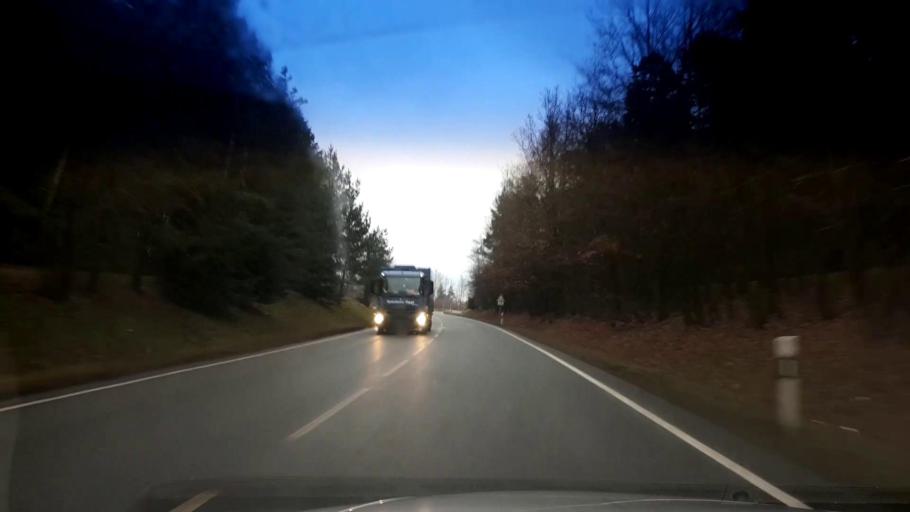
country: DE
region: Bavaria
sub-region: Upper Palatinate
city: Tirschenreuth
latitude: 49.8942
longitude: 12.3083
